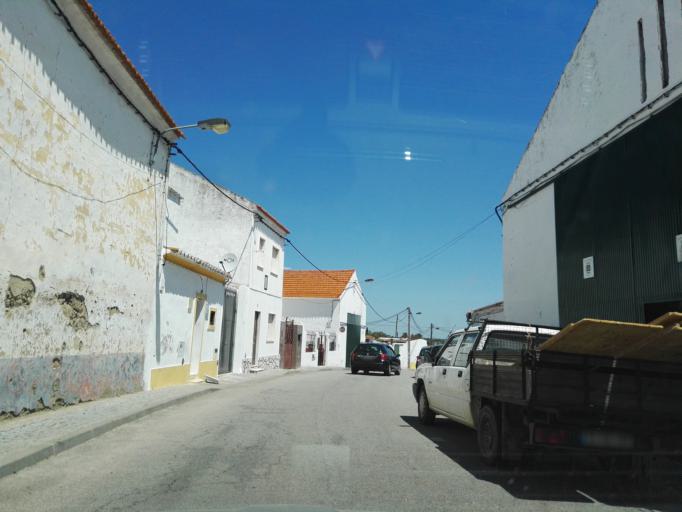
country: PT
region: Portalegre
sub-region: Arronches
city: Arronches
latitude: 39.0065
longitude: -7.2470
